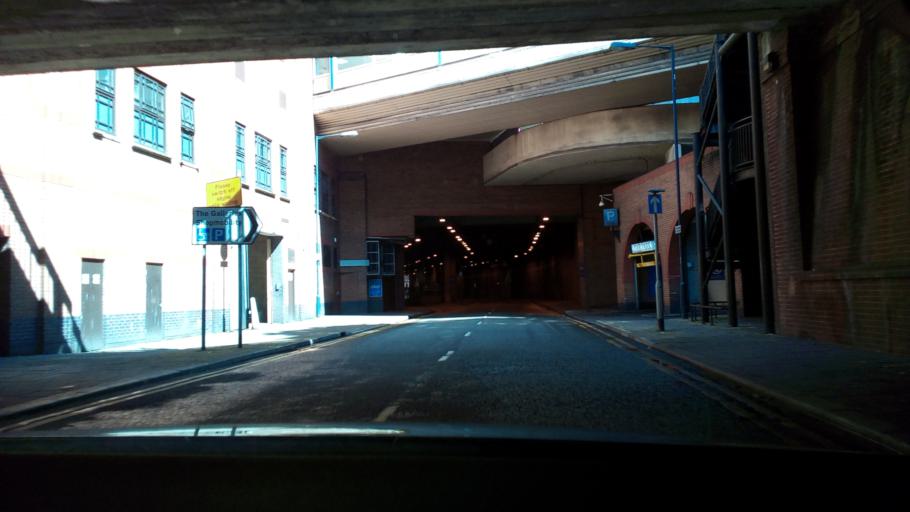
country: GB
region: England
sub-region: Bristol
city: Bristol
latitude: 51.4560
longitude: -2.5910
